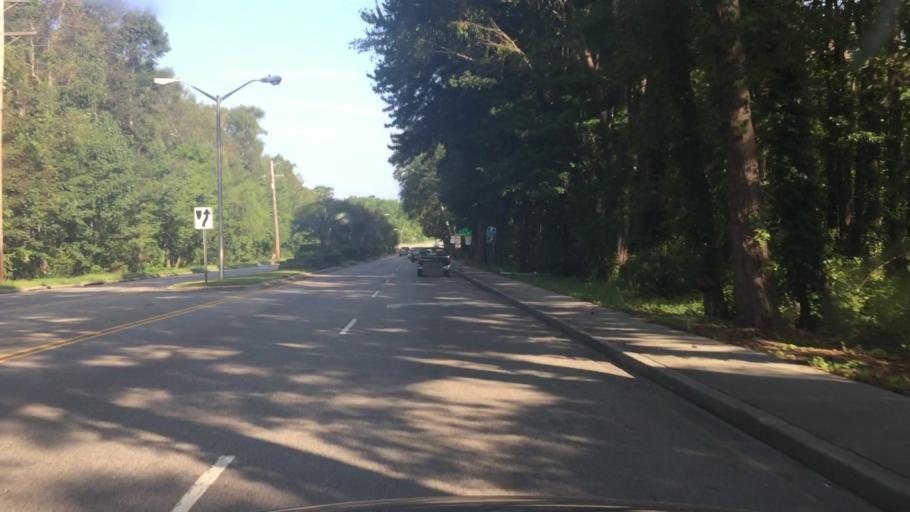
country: US
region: South Carolina
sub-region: Horry County
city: North Myrtle Beach
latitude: 33.8429
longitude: -78.6486
